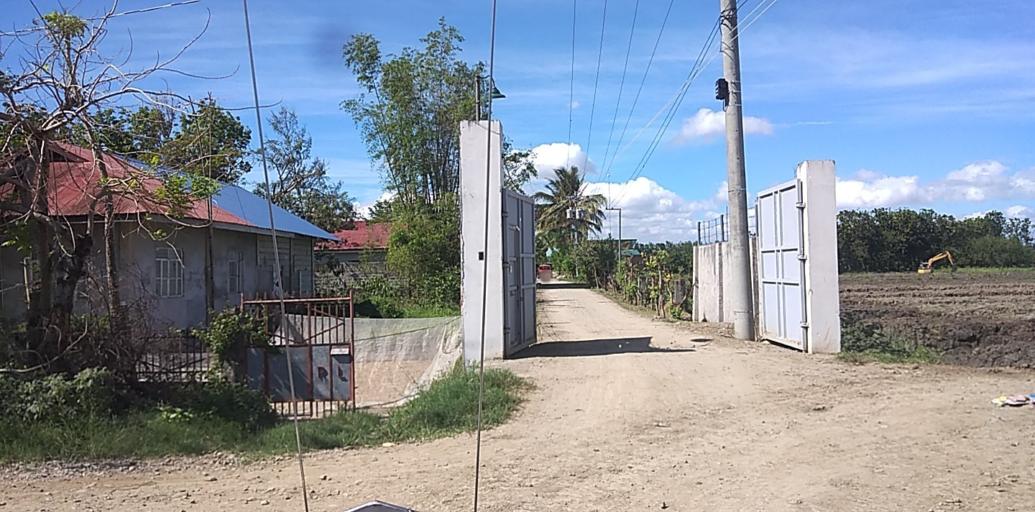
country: PH
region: Central Luzon
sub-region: Province of Pampanga
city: Candating
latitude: 15.1284
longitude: 120.8080
